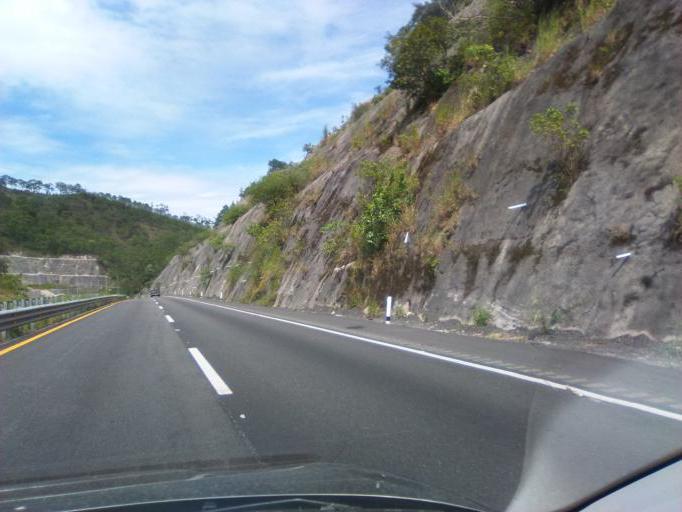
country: MX
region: Guerrero
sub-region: Chilpancingo de los Bravo
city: Acahuizotla
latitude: 17.3247
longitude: -99.4751
